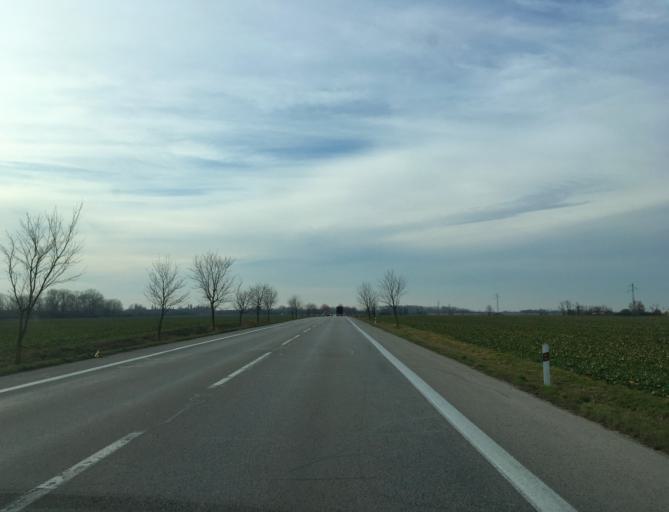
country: SK
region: Nitriansky
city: Sellye
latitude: 48.1500
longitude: 17.9576
